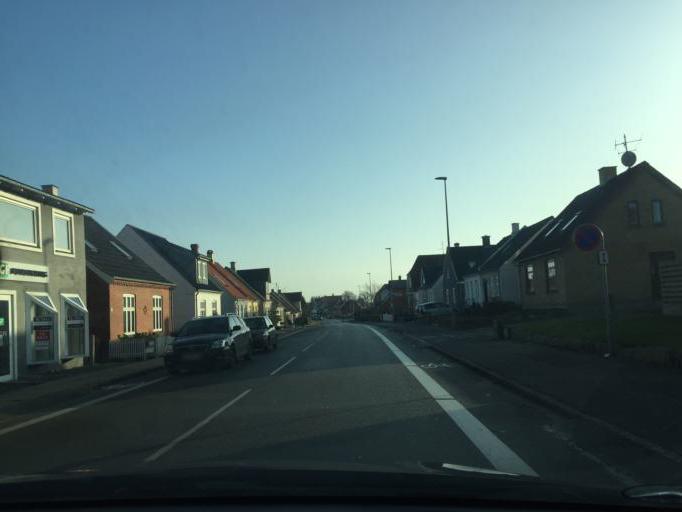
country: DK
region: South Denmark
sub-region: Faaborg-Midtfyn Kommune
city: Faaborg
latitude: 55.1034
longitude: 10.2269
